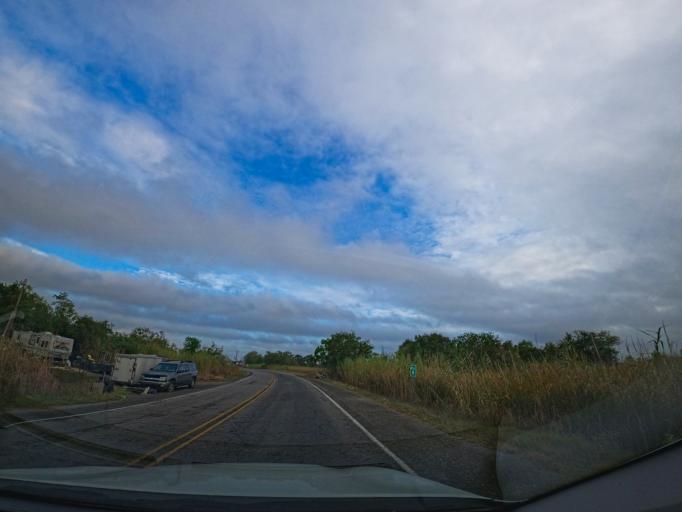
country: US
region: Louisiana
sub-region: Terrebonne Parish
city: Dulac
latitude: 29.3747
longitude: -90.7118
